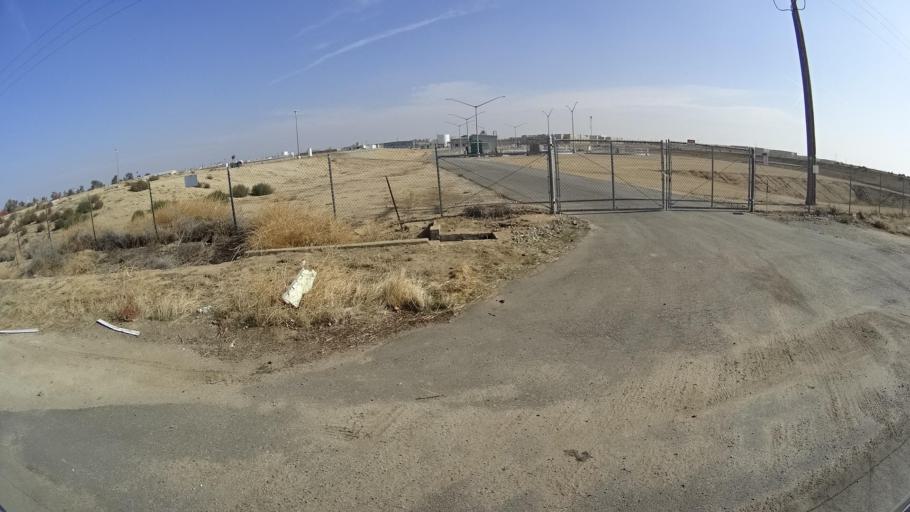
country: US
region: California
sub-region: Kern County
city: Greenacres
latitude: 35.5105
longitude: -119.1166
